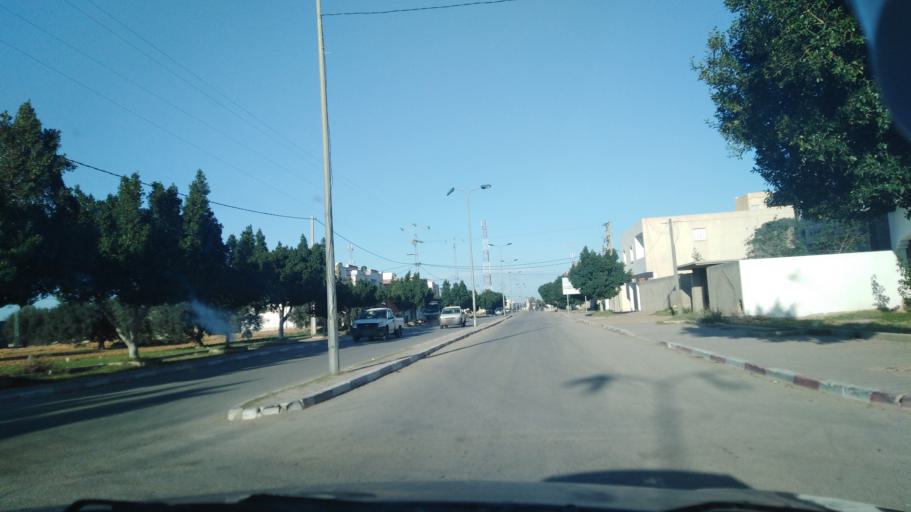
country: TN
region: Al Mahdiyah
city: Shurban
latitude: 34.9679
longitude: 10.3696
